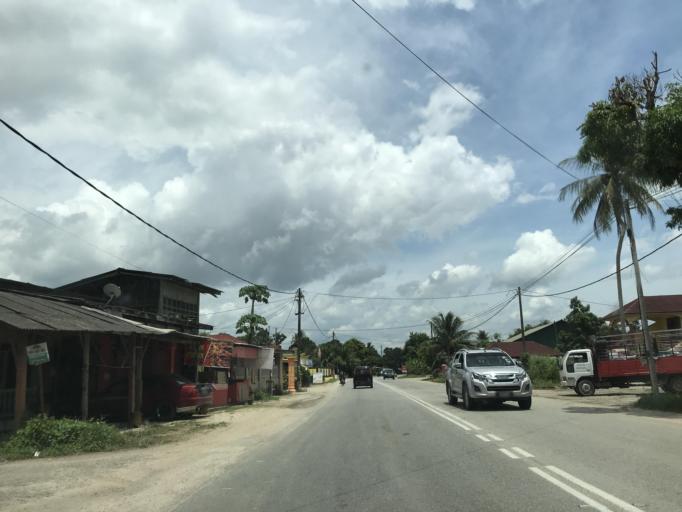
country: MY
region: Kelantan
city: Pasir Mas
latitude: 6.0545
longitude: 102.1930
